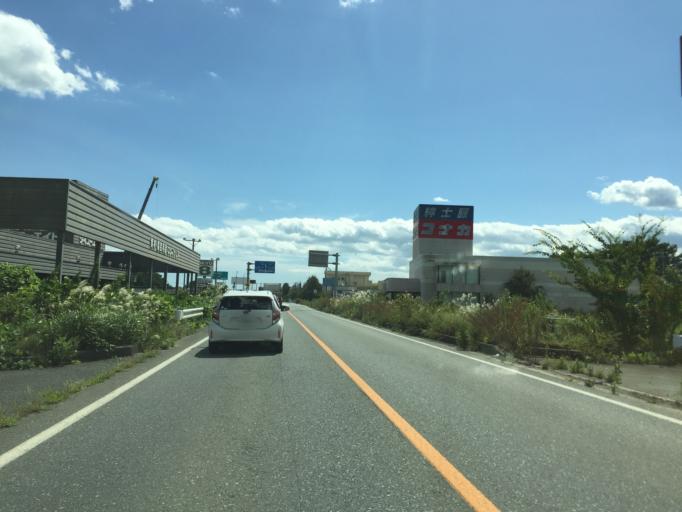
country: JP
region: Fukushima
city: Namie
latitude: 37.3590
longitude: 141.0101
